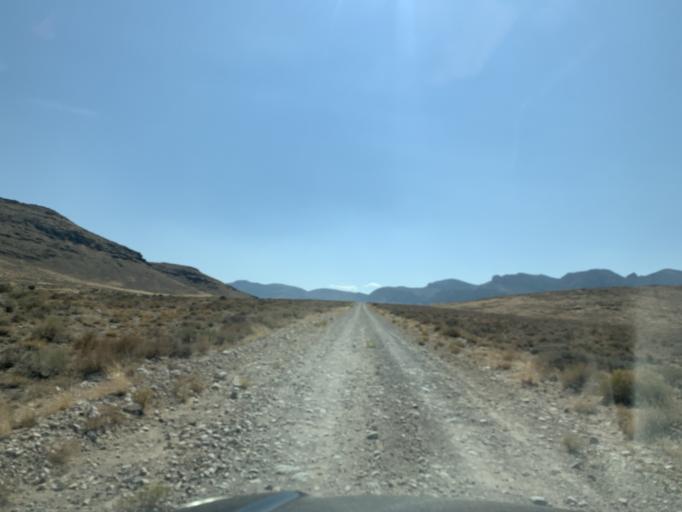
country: US
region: Utah
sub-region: Beaver County
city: Milford
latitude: 38.9797
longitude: -113.4482
